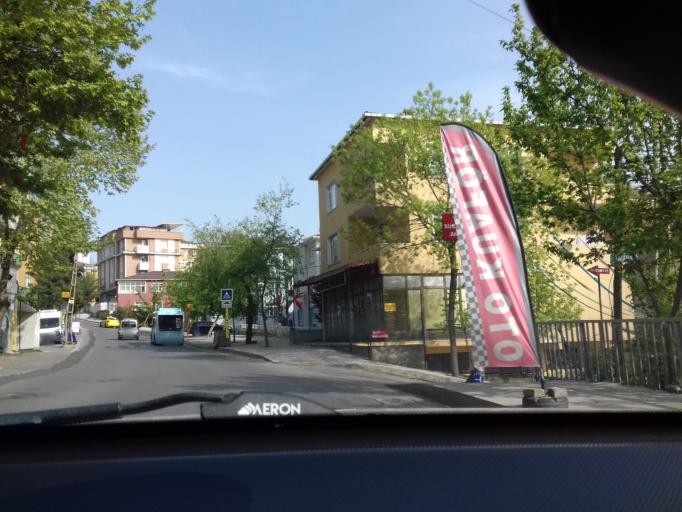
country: TR
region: Istanbul
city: Pendik
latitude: 40.9126
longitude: 29.2280
